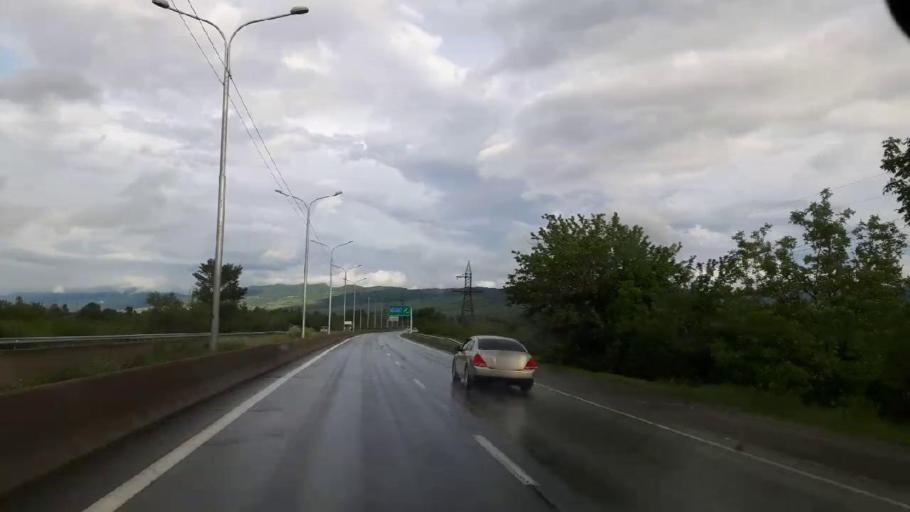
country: GE
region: Shida Kartli
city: Kaspi
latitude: 41.9178
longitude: 44.5521
